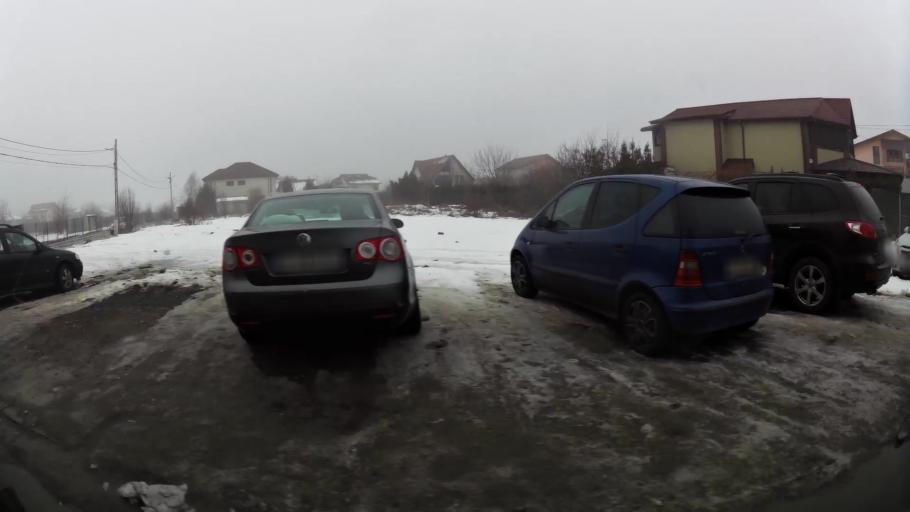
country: RO
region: Ilfov
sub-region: Comuna Chiajna
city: Rosu
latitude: 44.4500
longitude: 25.9920
